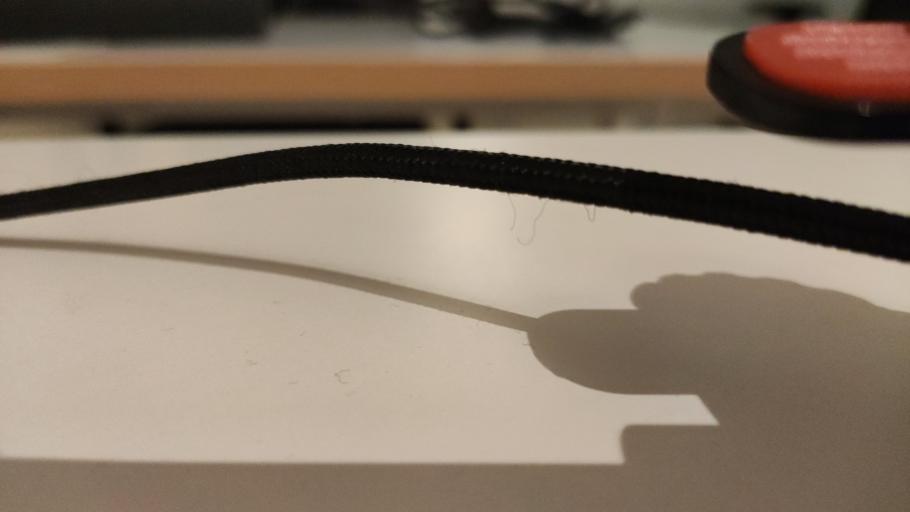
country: RU
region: Moskovskaya
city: Il'inskiy Pogost
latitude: 55.5227
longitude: 38.8719
